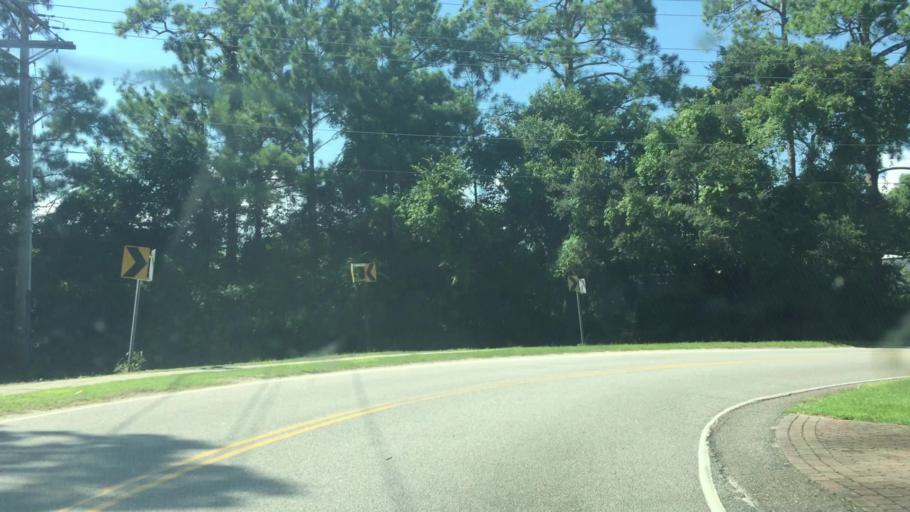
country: US
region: South Carolina
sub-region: Horry County
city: North Myrtle Beach
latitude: 33.8307
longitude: -78.6691
